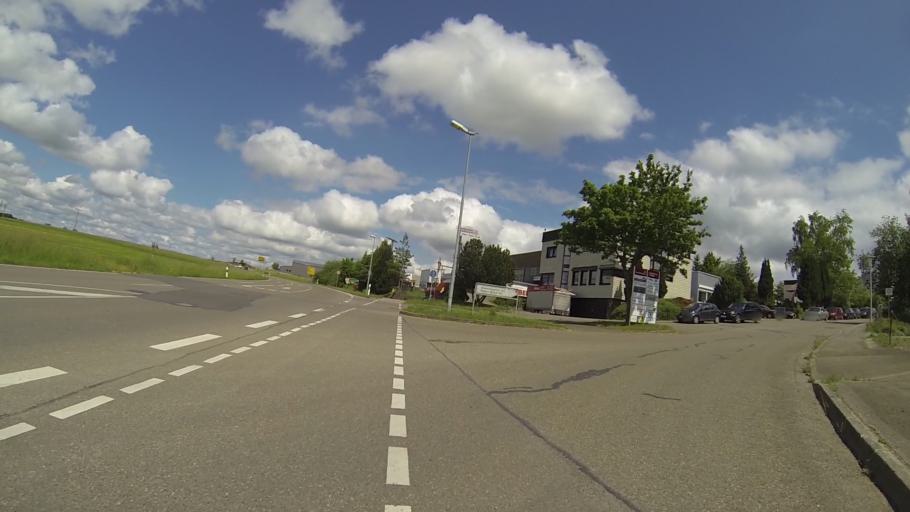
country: DE
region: Baden-Wuerttemberg
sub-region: Regierungsbezirk Stuttgart
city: Waldstetten
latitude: 48.7719
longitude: 9.8323
